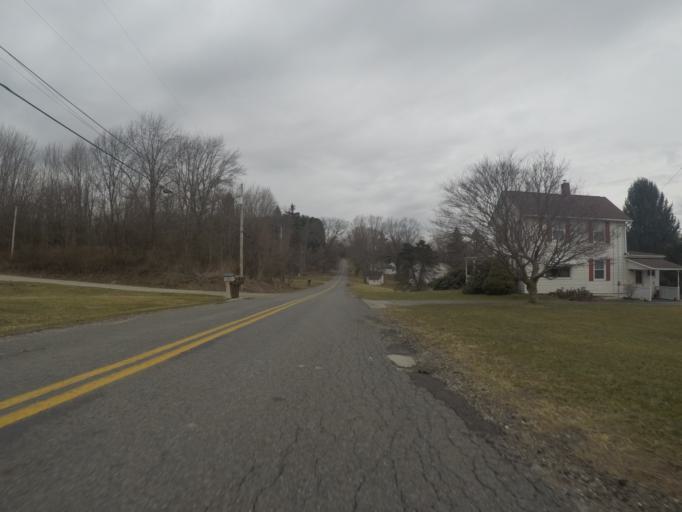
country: US
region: Ohio
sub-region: Portage County
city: Ravenna
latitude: 41.1815
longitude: -81.2965
